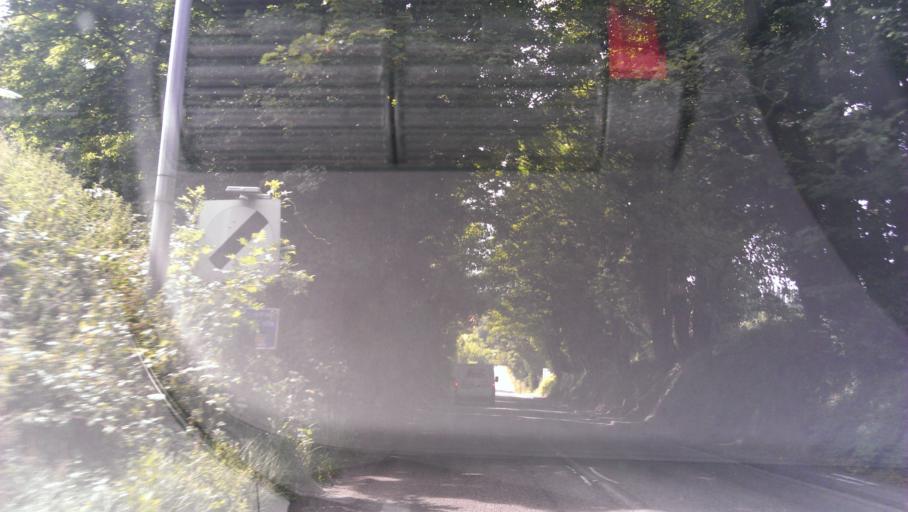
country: GB
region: England
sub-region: Kent
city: Faversham
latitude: 51.3143
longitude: 0.8610
